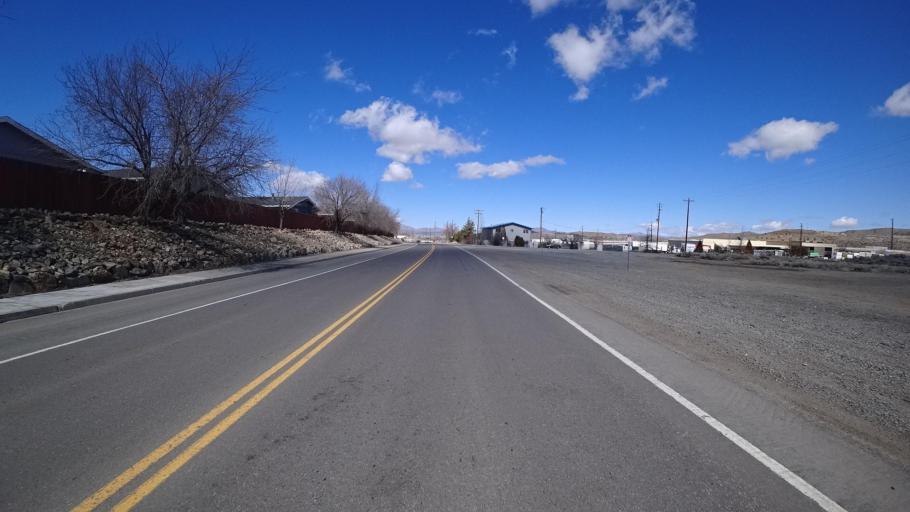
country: US
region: Nevada
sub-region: Washoe County
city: Golden Valley
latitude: 39.5937
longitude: -119.8364
